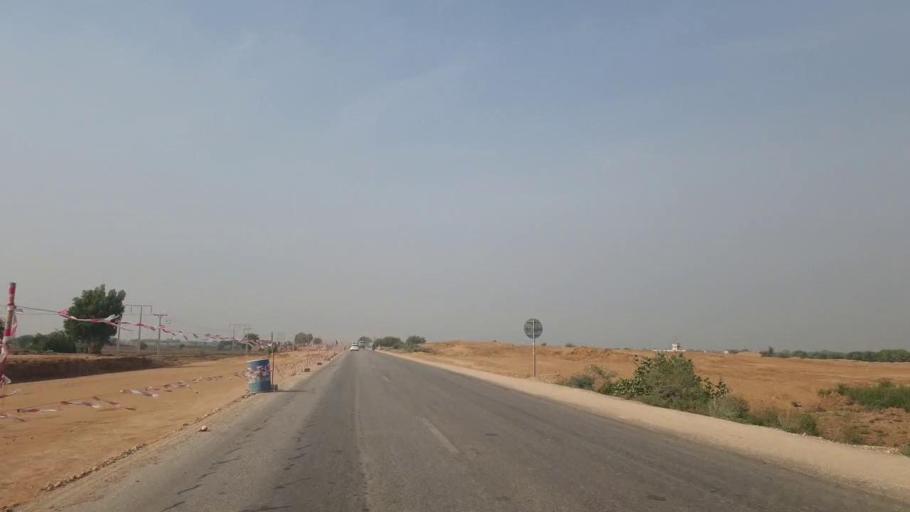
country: PK
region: Sindh
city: Sann
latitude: 26.1300
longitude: 68.0499
